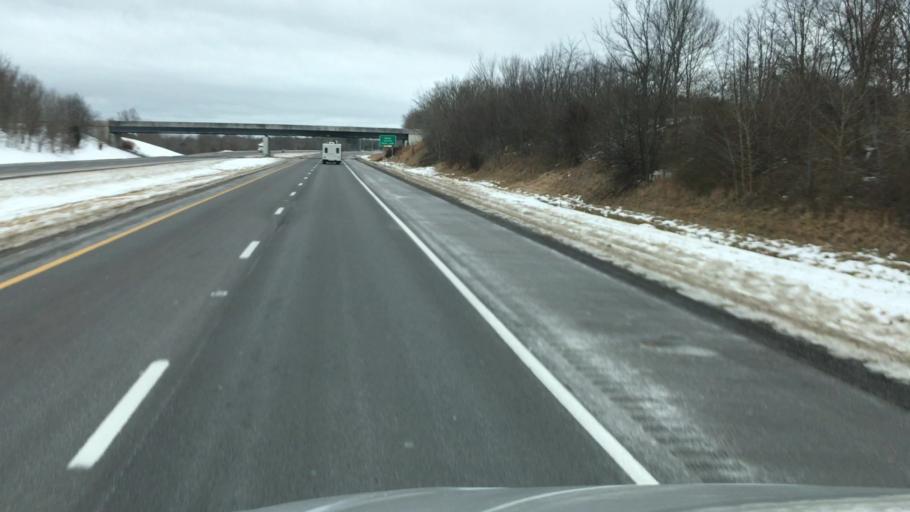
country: US
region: Kentucky
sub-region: Lyon County
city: Eddyville
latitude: 37.0639
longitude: -88.1722
